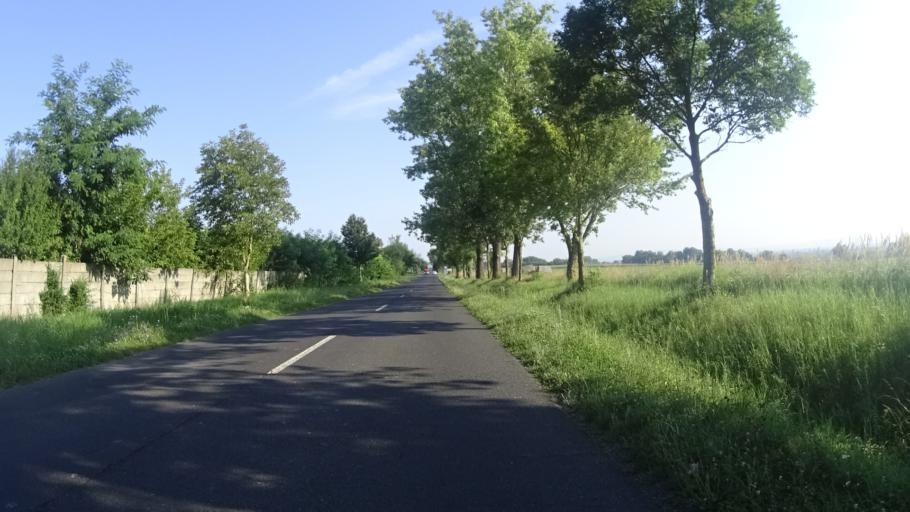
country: HU
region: Zala
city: Sarmellek
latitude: 46.6880
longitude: 17.1687
